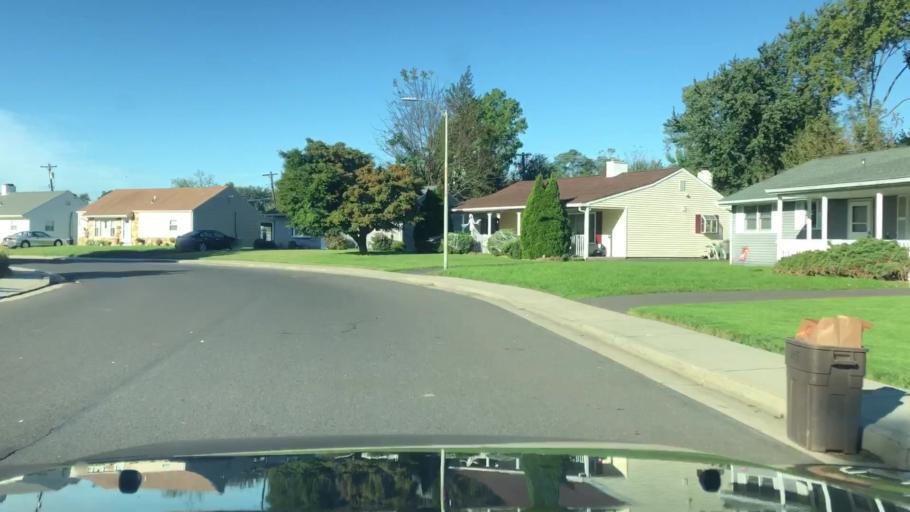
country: US
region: Pennsylvania
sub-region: Bucks County
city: Fairless Hills
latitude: 40.1805
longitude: -74.8636
